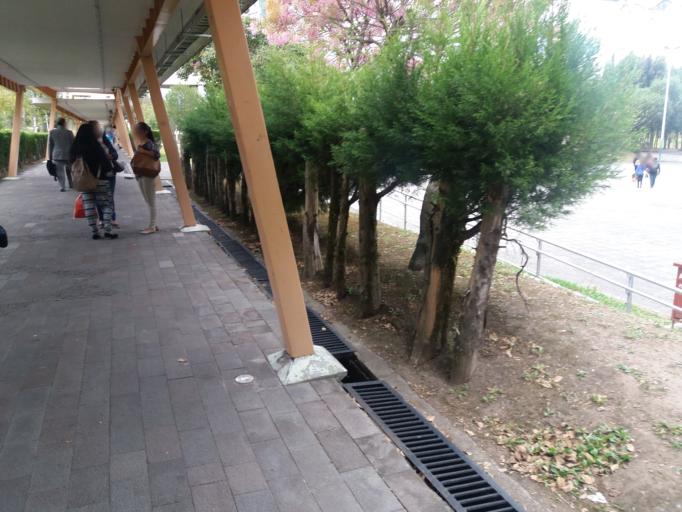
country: EC
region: Pichincha
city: Sangolqui
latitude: -0.3142
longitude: -78.4449
